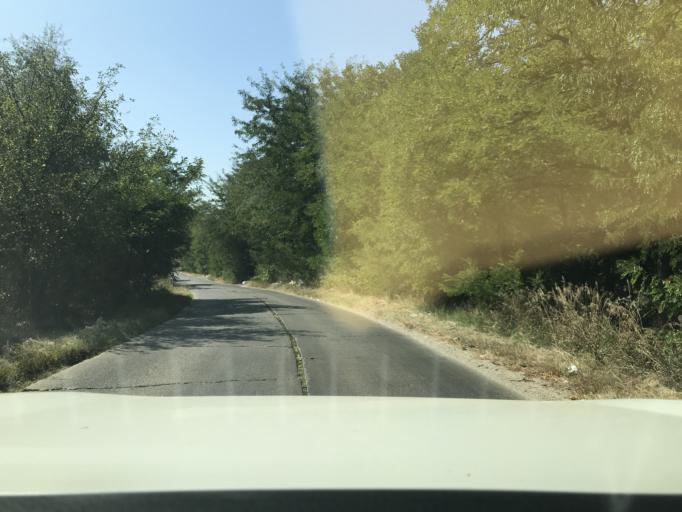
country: RO
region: Olt
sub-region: Municipiul Slatina
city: Slatina
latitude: 44.4116
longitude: 24.3597
